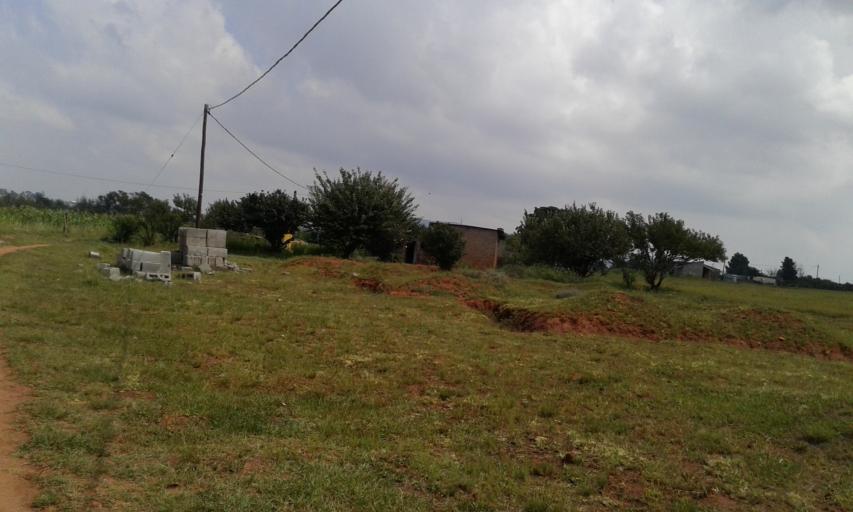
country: LS
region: Maseru
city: Maseru
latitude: -29.4308
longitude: 27.5750
